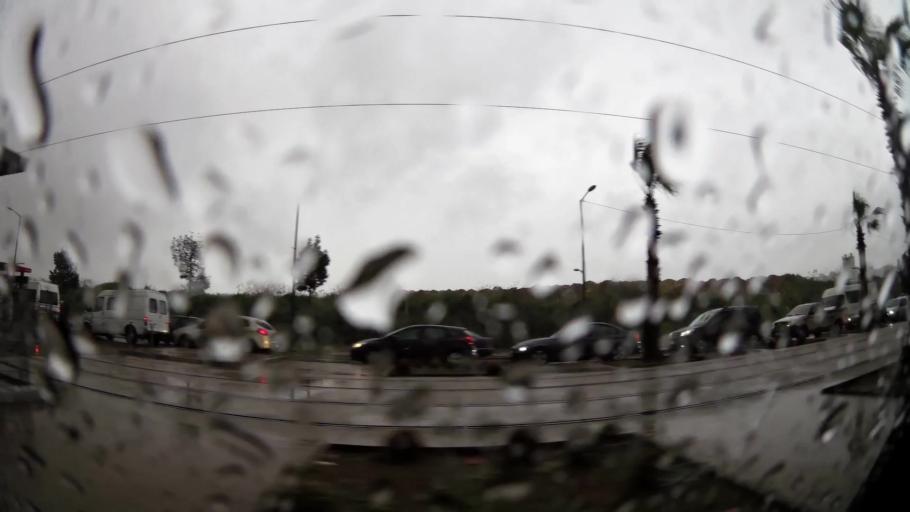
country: MA
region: Grand Casablanca
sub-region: Mediouna
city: Tit Mellil
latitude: 33.5826
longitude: -7.5083
